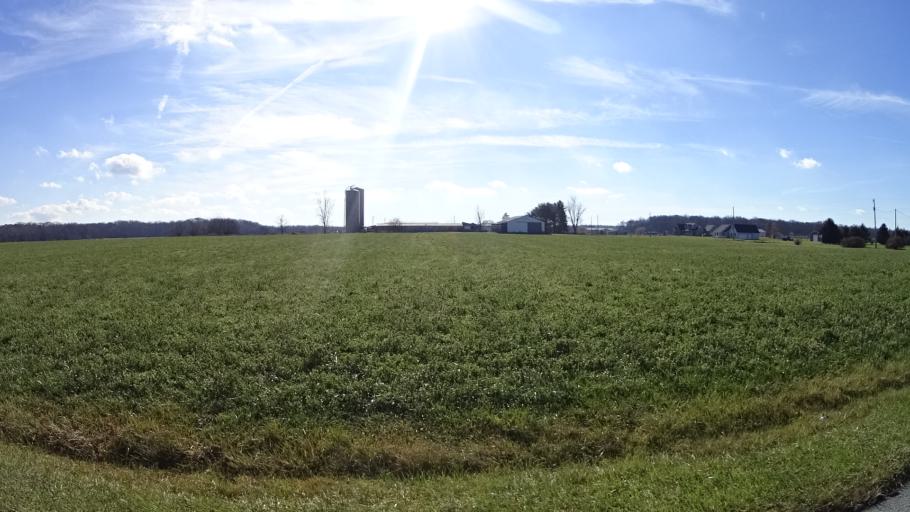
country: US
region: Ohio
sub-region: Lorain County
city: Wellington
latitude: 41.0844
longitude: -82.1802
